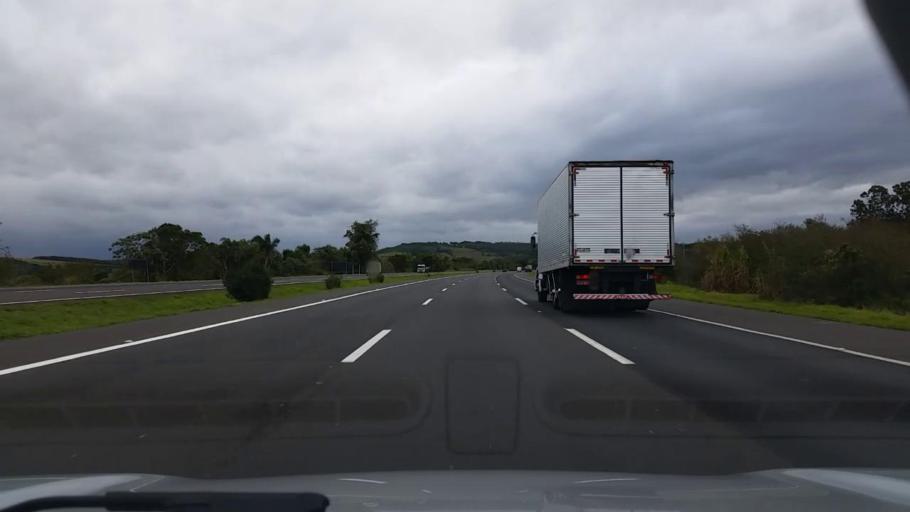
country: BR
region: Rio Grande do Sul
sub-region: Osorio
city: Osorio
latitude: -29.8888
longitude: -50.4591
